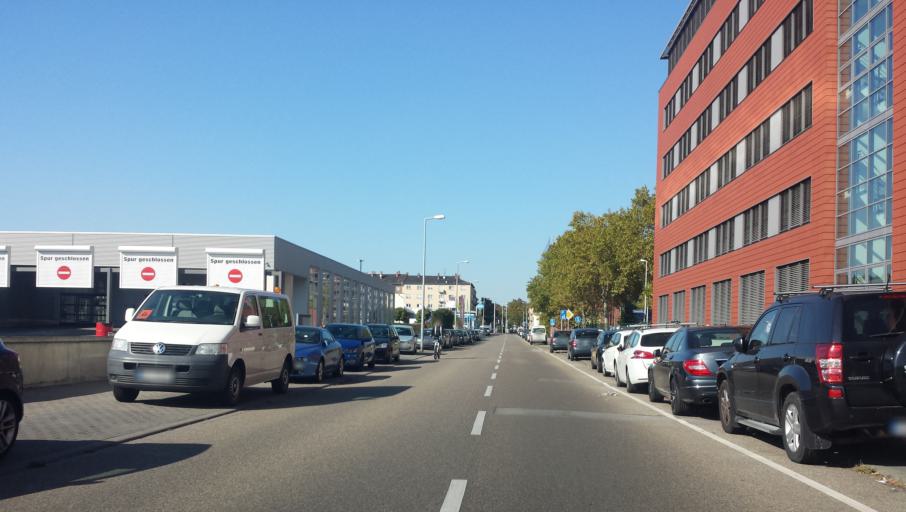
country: DE
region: Baden-Wuerttemberg
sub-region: Karlsruhe Region
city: Mannheim
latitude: 49.4739
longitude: 8.4894
